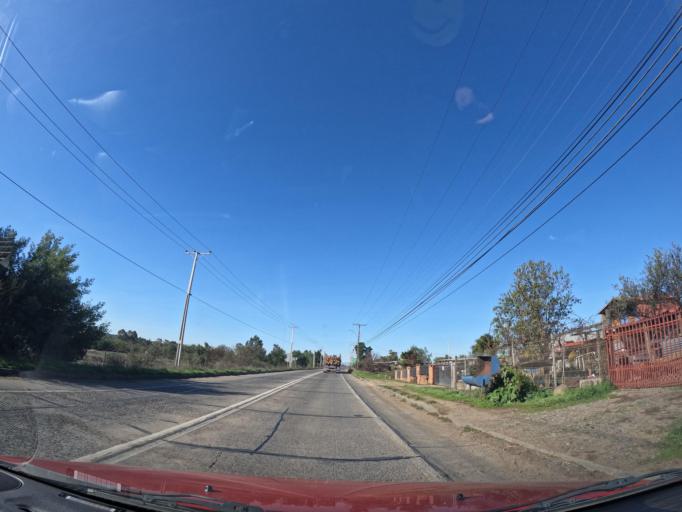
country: CL
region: Maule
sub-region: Provincia de Cauquenes
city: Cauquenes
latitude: -35.9575
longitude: -72.2766
